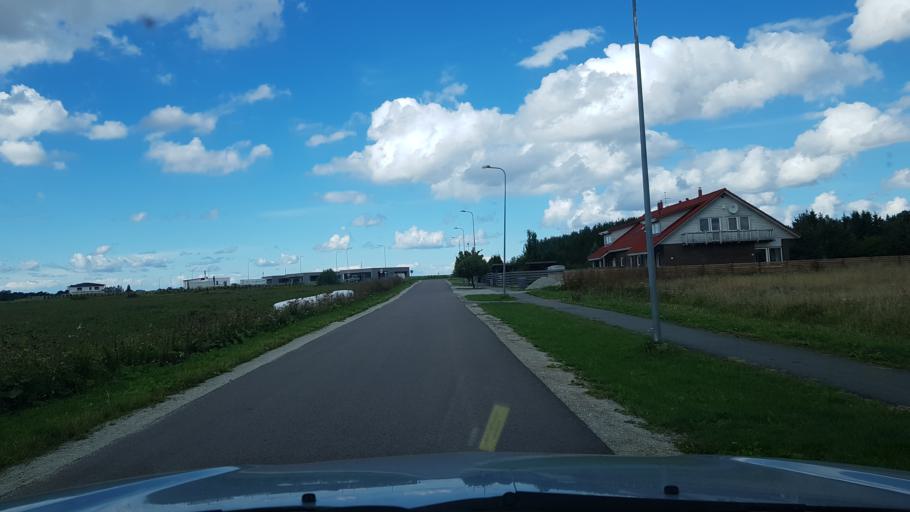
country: EE
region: Harju
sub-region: Kiili vald
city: Kiili
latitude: 59.3749
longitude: 24.8138
